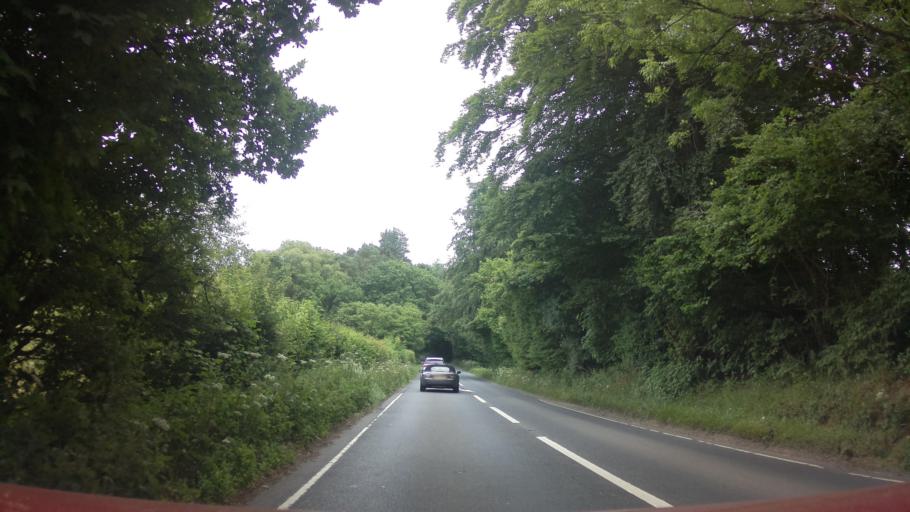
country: GB
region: England
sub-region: Devon
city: Newton Poppleford
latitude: 50.7052
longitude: -3.3484
